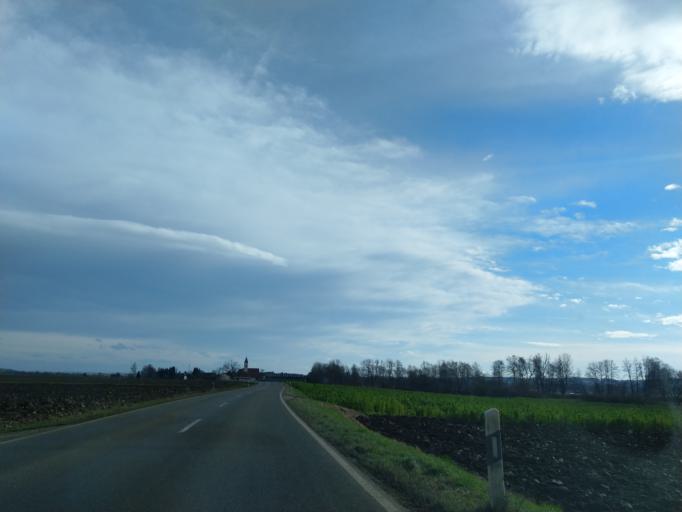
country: DE
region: Bavaria
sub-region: Lower Bavaria
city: Rossbach
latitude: 48.6306
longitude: 12.9473
